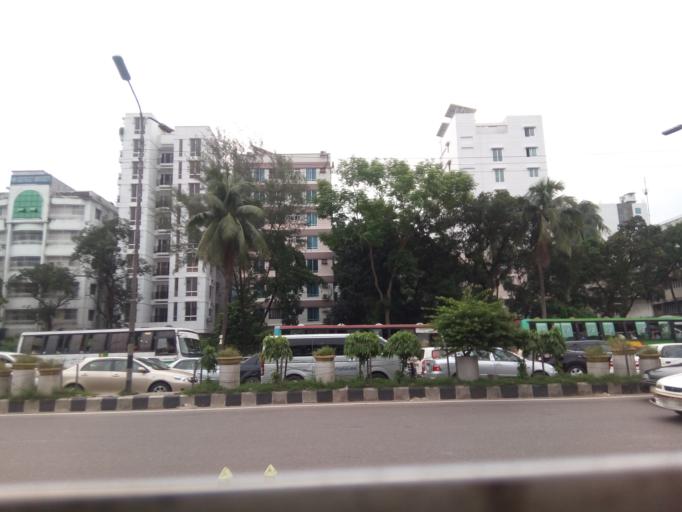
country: BD
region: Dhaka
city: Paltan
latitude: 23.7952
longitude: 90.4010
